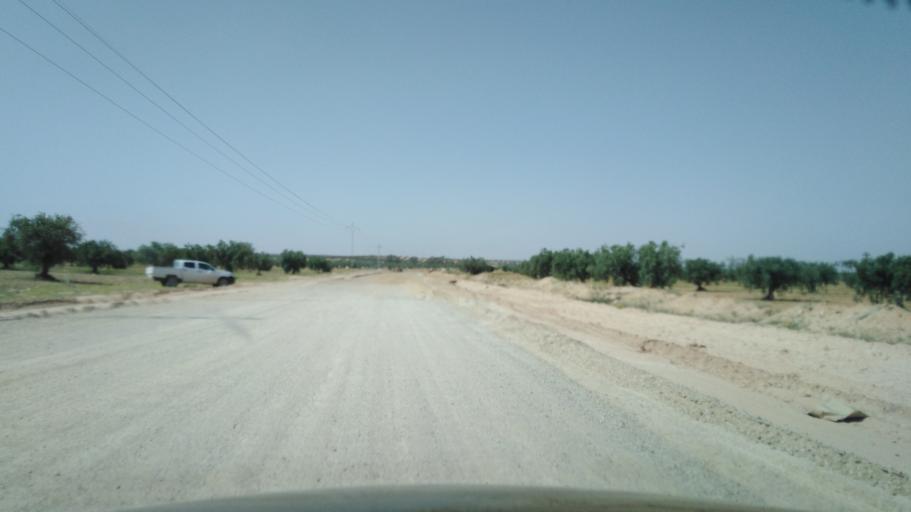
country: TN
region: Safaqis
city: Sfax
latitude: 34.6962
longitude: 10.4781
